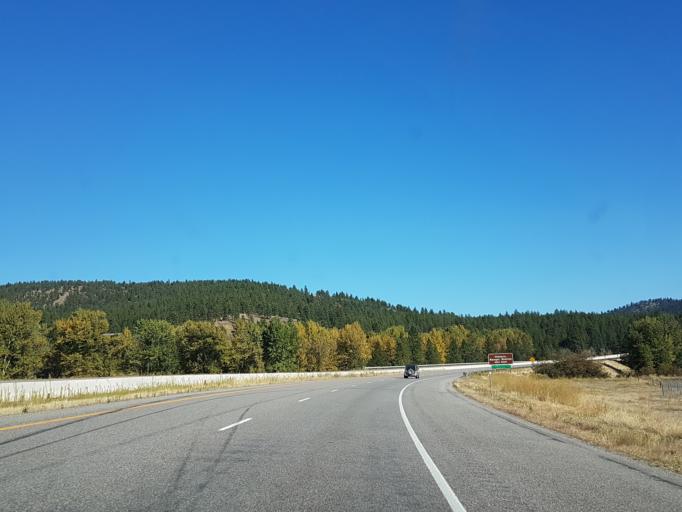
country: US
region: Montana
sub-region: Missoula County
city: Frenchtown
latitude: 47.0233
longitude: -114.3900
